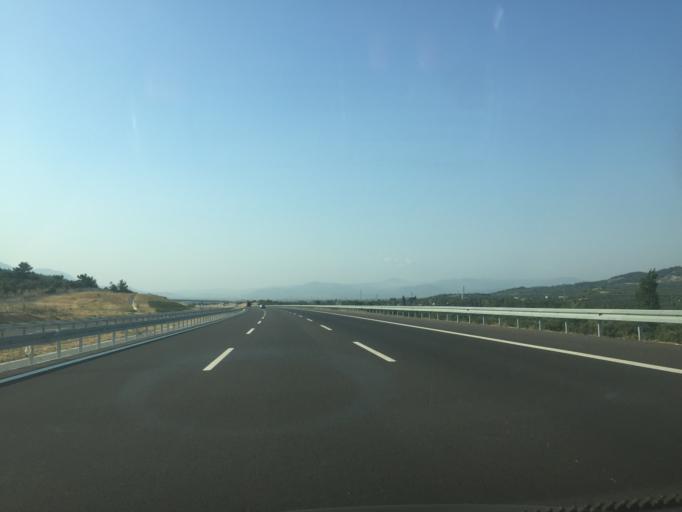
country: TR
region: Manisa
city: Zeytinliova
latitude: 39.0308
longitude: 27.7492
